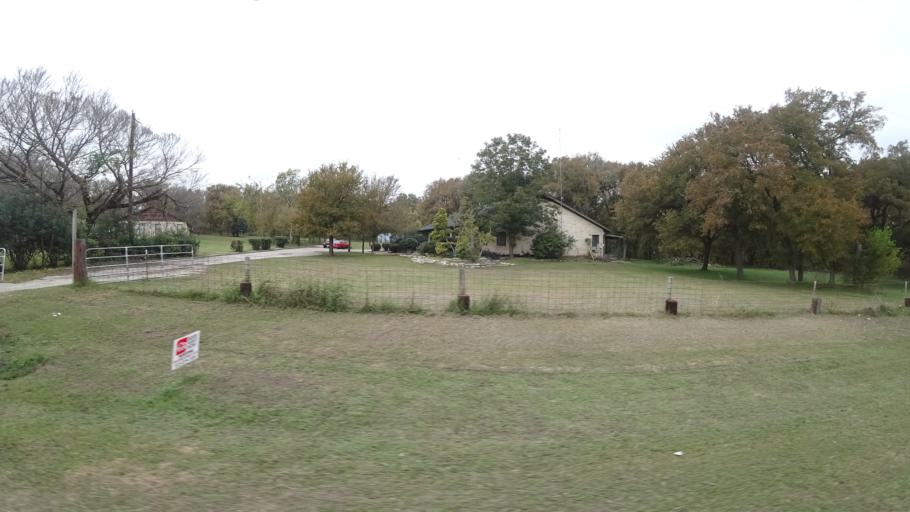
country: US
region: Texas
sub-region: Travis County
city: Pflugerville
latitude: 30.3956
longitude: -97.5946
